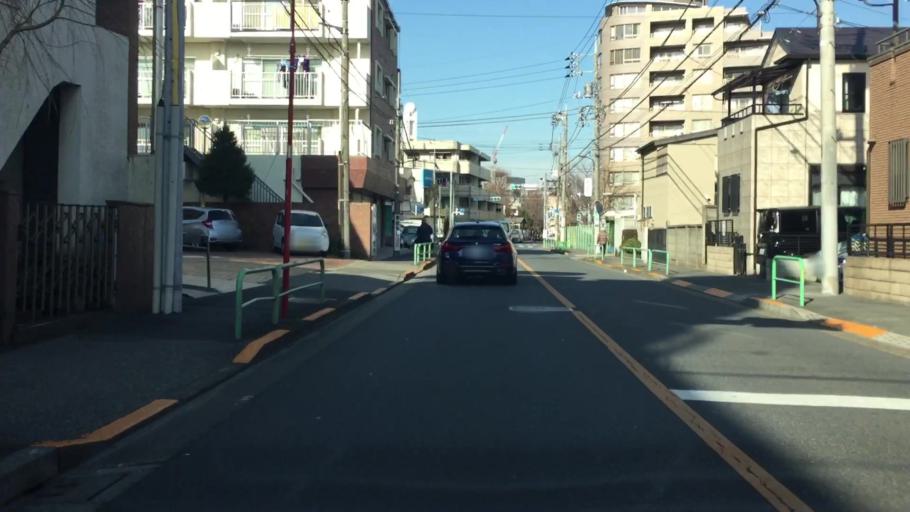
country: JP
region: Saitama
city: Wako
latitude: 35.7578
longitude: 139.6615
